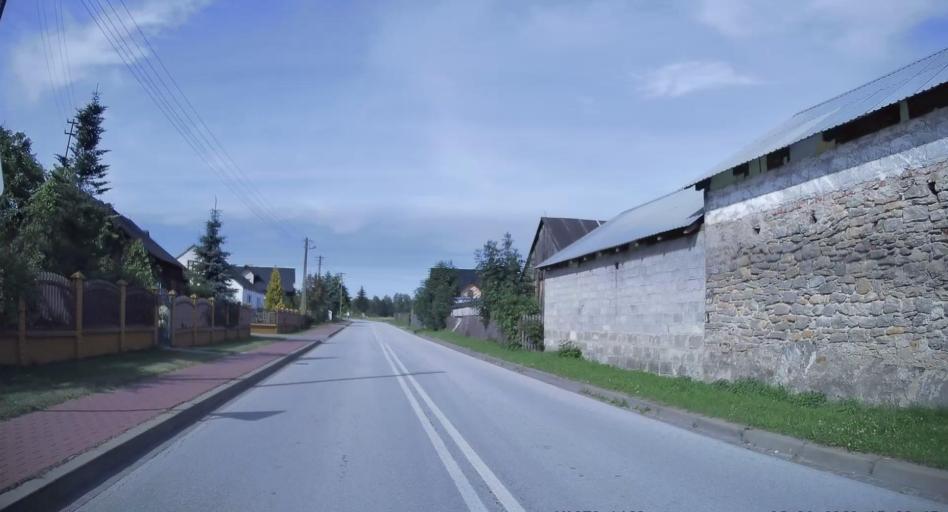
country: PL
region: Lodz Voivodeship
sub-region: Powiat opoczynski
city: Mniszkow
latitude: 51.3325
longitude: 20.0304
